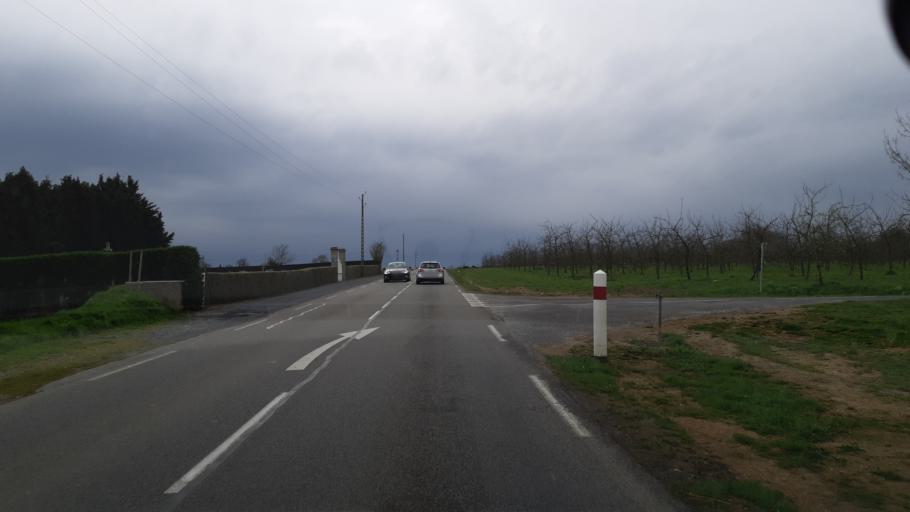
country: FR
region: Lower Normandy
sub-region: Departement de la Manche
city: Percy
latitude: 48.9599
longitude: -1.1759
